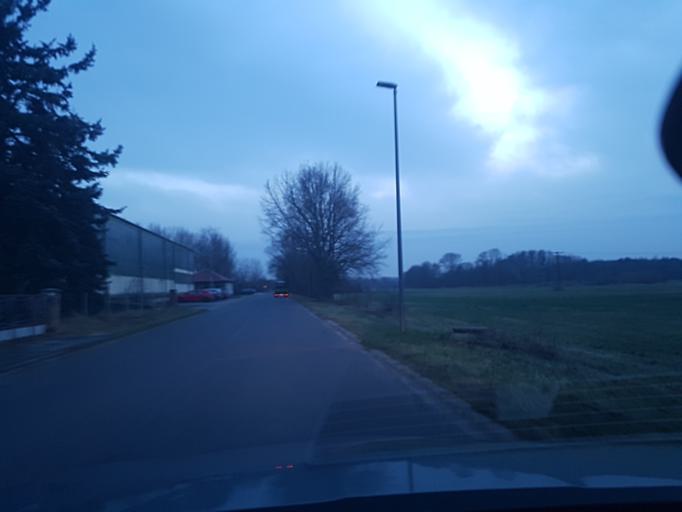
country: DE
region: Brandenburg
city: Doberlug-Kirchhain
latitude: 51.6046
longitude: 13.5470
